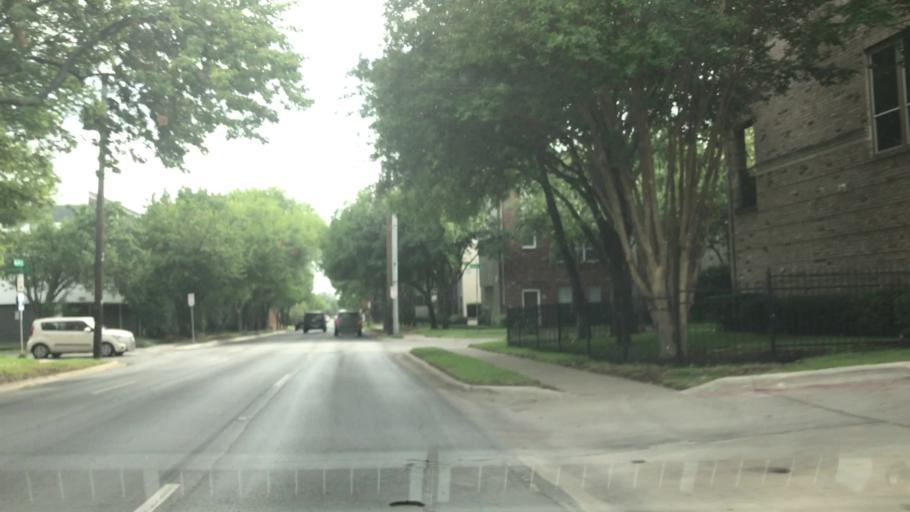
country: US
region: Texas
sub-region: Dallas County
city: Highland Park
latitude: 32.8186
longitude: -96.8091
